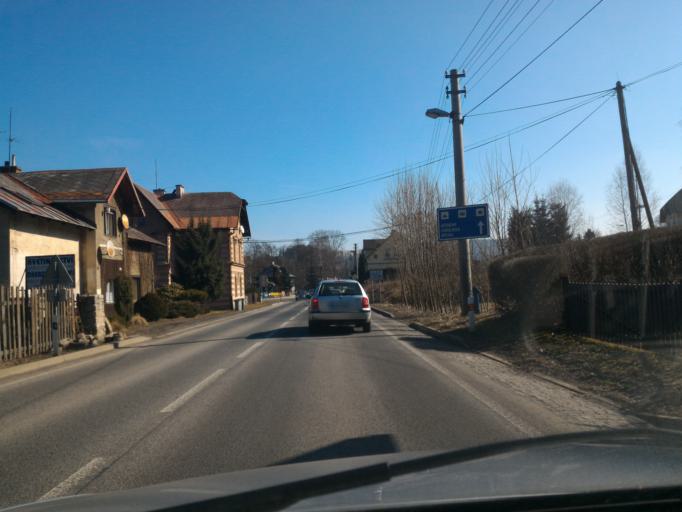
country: CZ
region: Liberecky
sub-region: Okres Jablonec nad Nisou
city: Smrzovka
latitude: 50.7359
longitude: 15.2758
